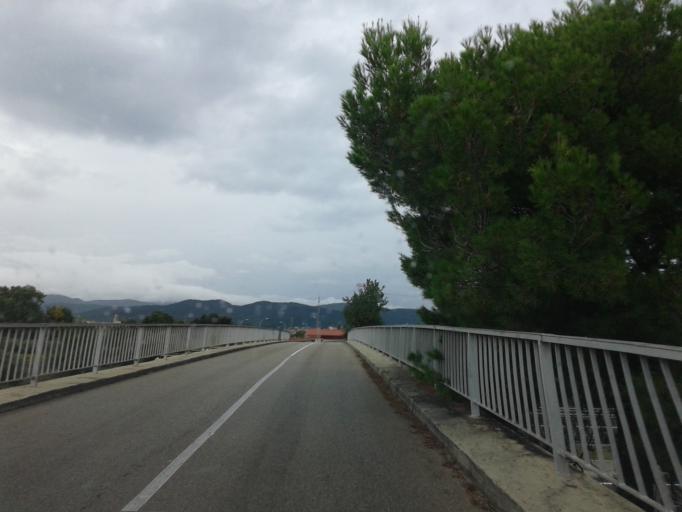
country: ES
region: Catalonia
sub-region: Provincia de Tarragona
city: Sant Jaume dels Domenys
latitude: 41.2782
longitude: 1.5637
